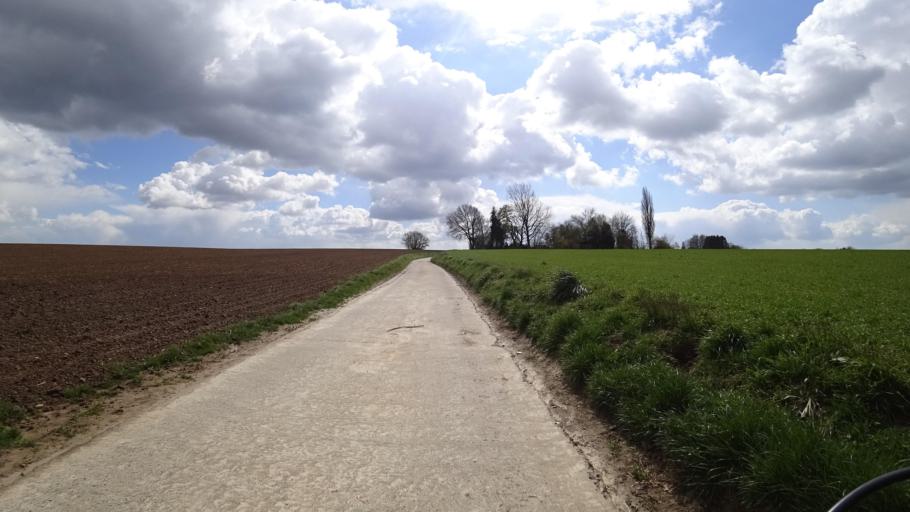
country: BE
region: Wallonia
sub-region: Province du Brabant Wallon
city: Chaumont-Gistoux
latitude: 50.6572
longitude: 4.7207
